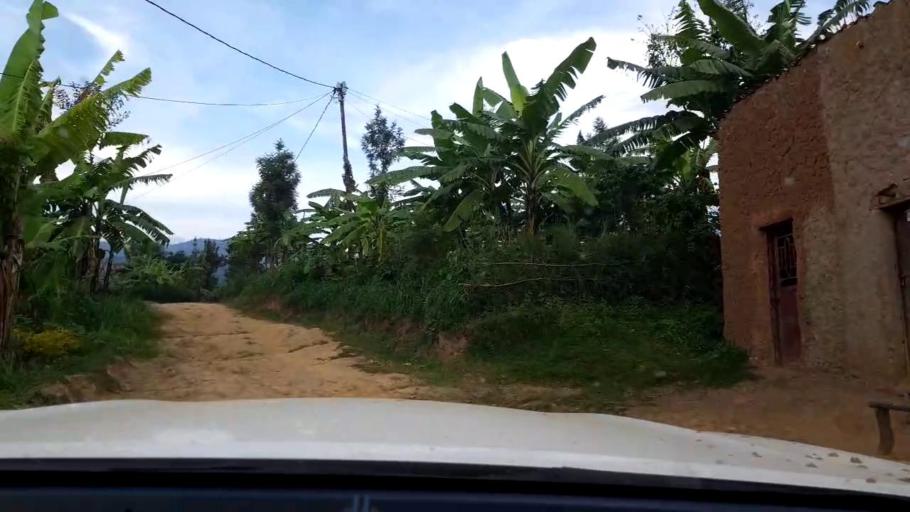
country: RW
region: Western Province
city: Kibuye
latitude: -2.0054
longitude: 29.3721
